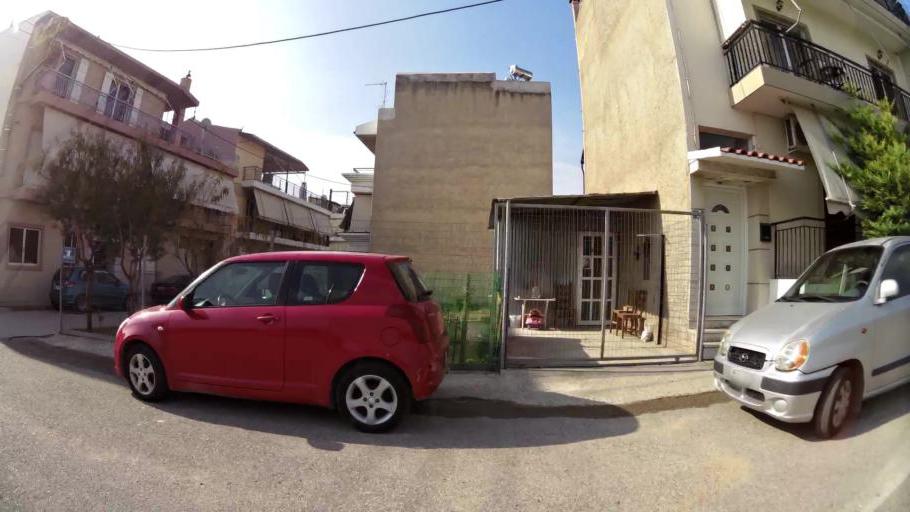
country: GR
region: Attica
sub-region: Nomarchia Athinas
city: Kamateron
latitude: 38.0490
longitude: 23.7038
